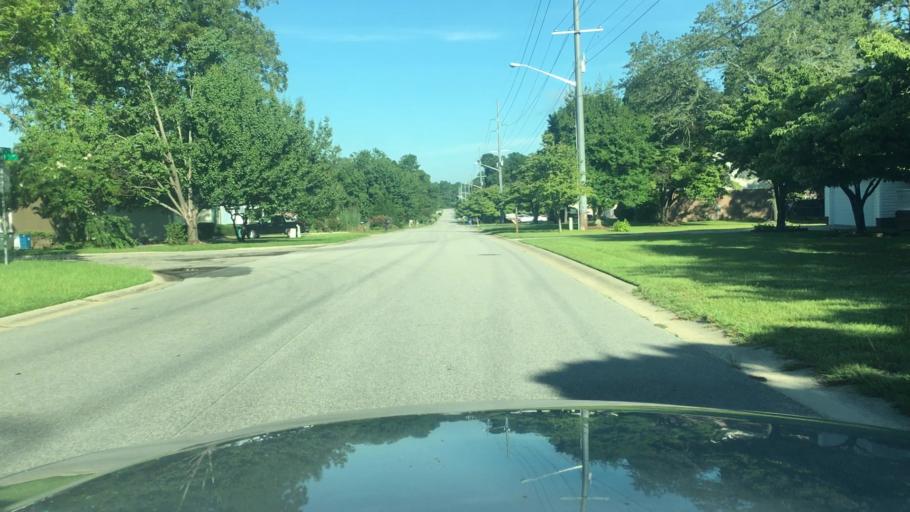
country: US
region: North Carolina
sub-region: Cumberland County
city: Fayetteville
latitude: 35.1294
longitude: -78.8842
